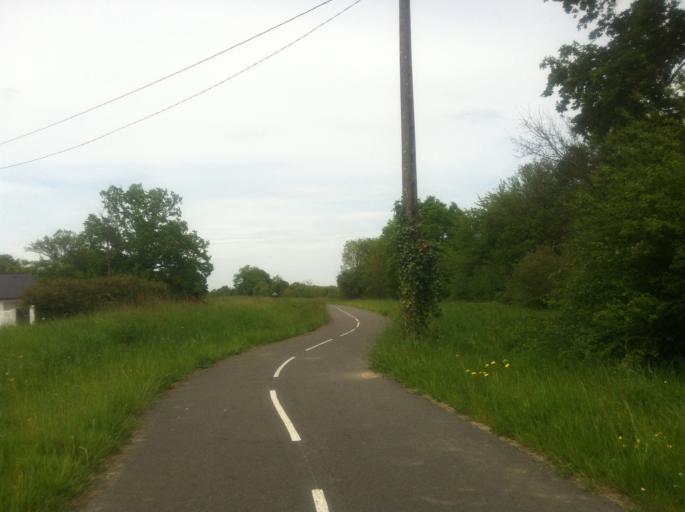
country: FR
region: Brittany
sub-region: Departement d'Ille-et-Vilaine
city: Chartres-de-Bretagne
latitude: 48.0305
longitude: -1.7249
